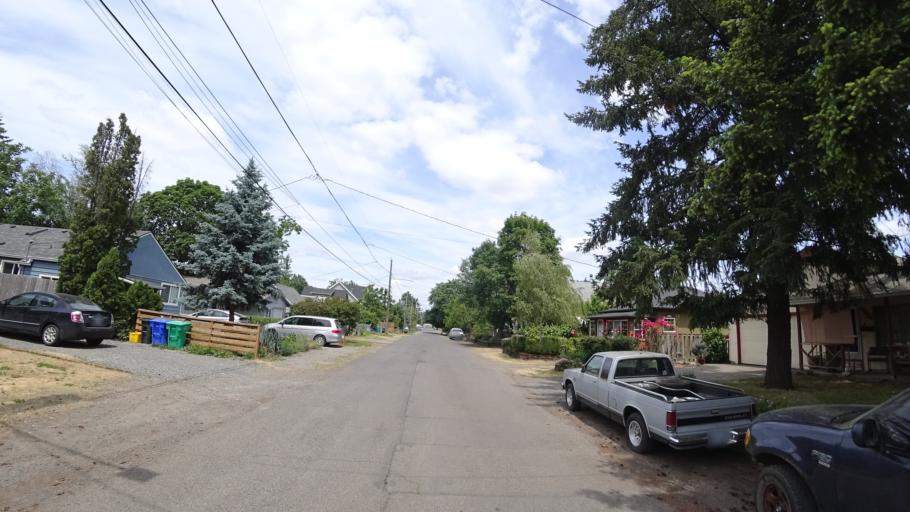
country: US
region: Oregon
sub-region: Multnomah County
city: Lents
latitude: 45.4722
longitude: -122.5933
